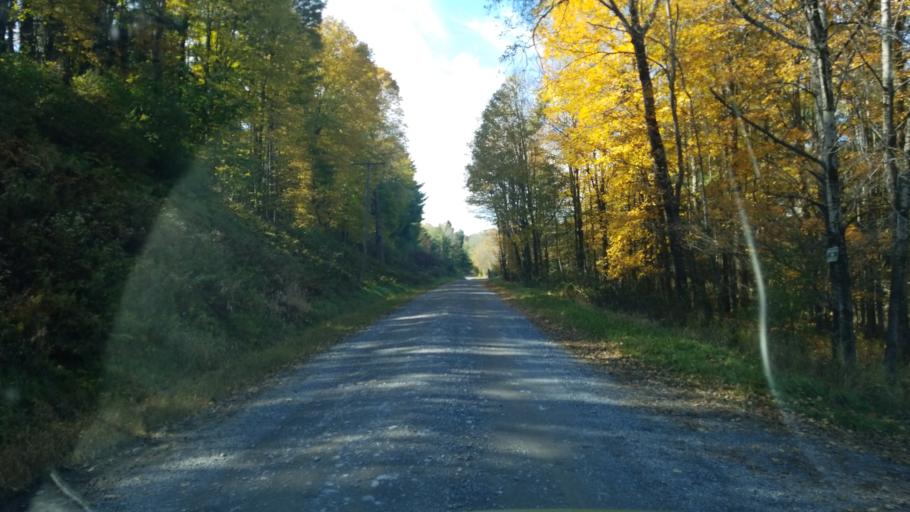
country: US
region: Pennsylvania
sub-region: Jefferson County
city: Falls Creek
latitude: 41.1919
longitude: -78.7906
